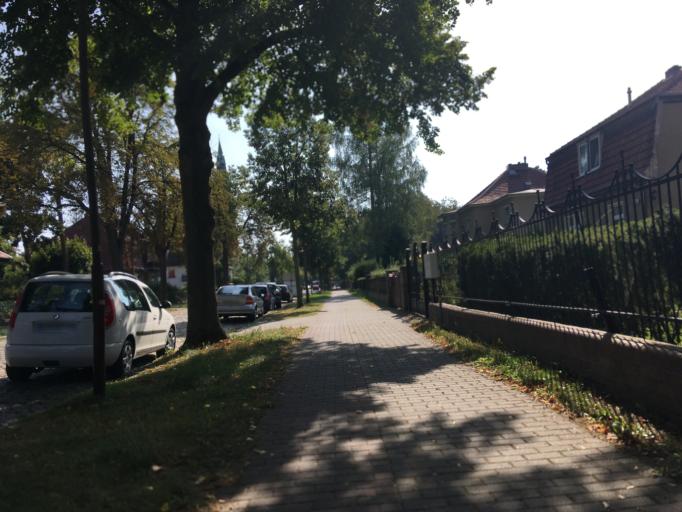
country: DE
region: Brandenburg
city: Zeuthen
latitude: 52.3767
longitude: 13.6174
